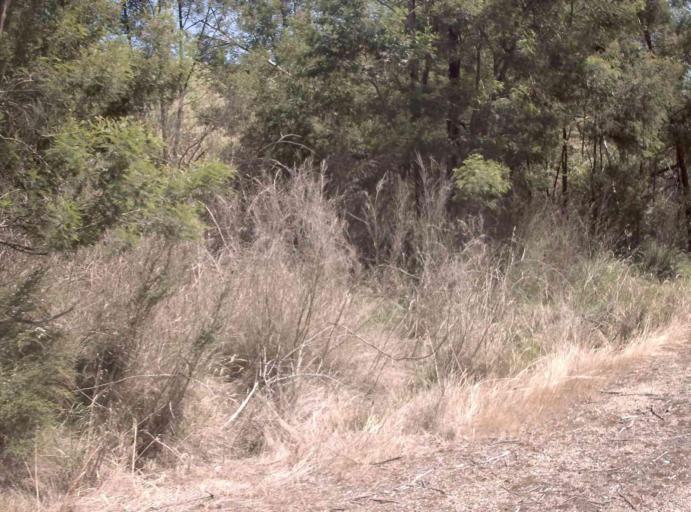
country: AU
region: Victoria
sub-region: East Gippsland
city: Lakes Entrance
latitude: -37.4037
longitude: 148.2113
